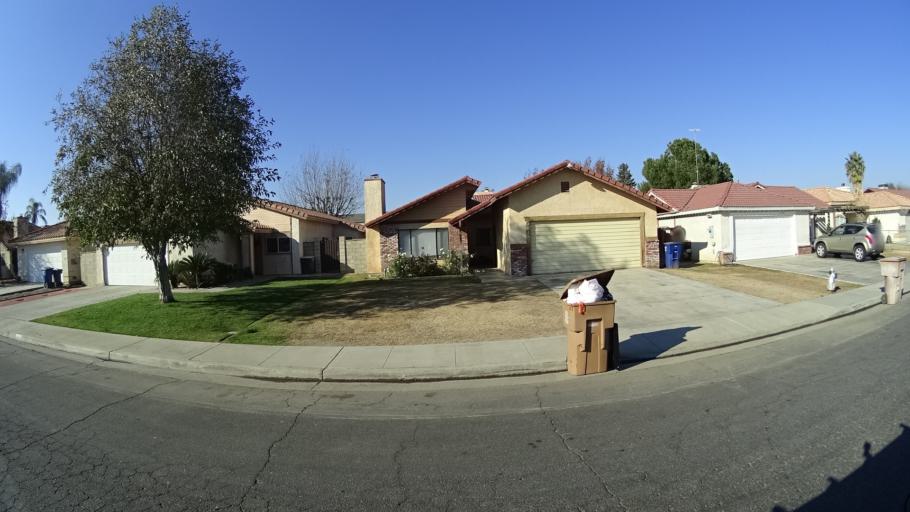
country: US
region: California
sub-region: Kern County
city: Greenfield
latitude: 35.3080
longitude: -119.0103
